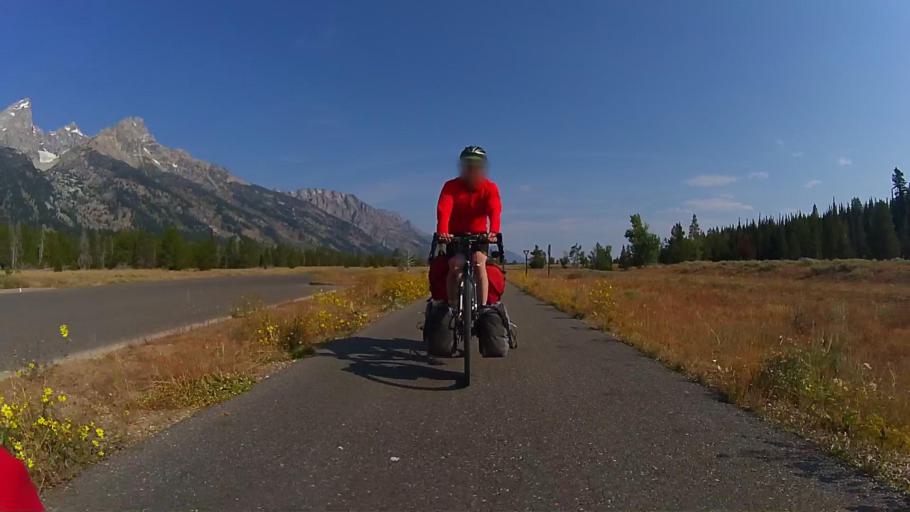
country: US
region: Wyoming
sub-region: Teton County
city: Moose Wilson Road
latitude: 43.7132
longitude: -110.7277
